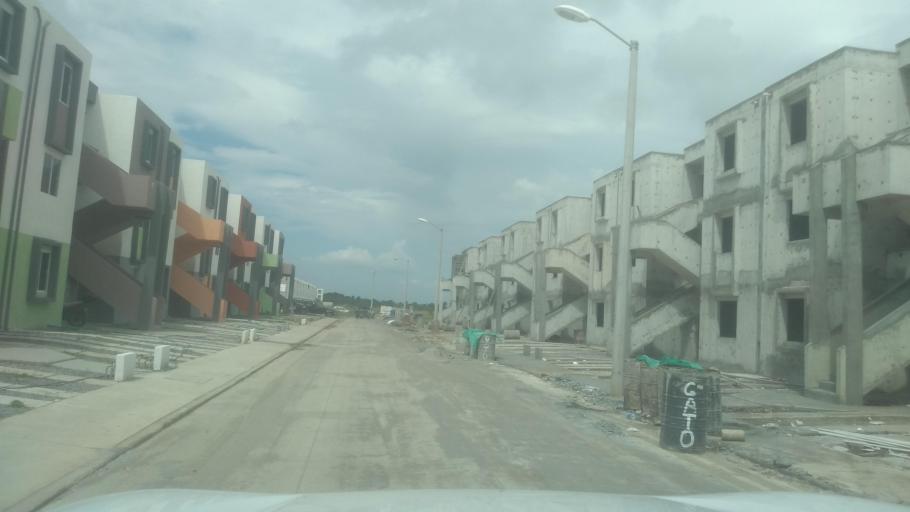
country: MX
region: Veracruz
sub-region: Medellin
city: Fraccionamiento Arboledas San Ramon
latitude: 19.0936
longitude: -96.1678
